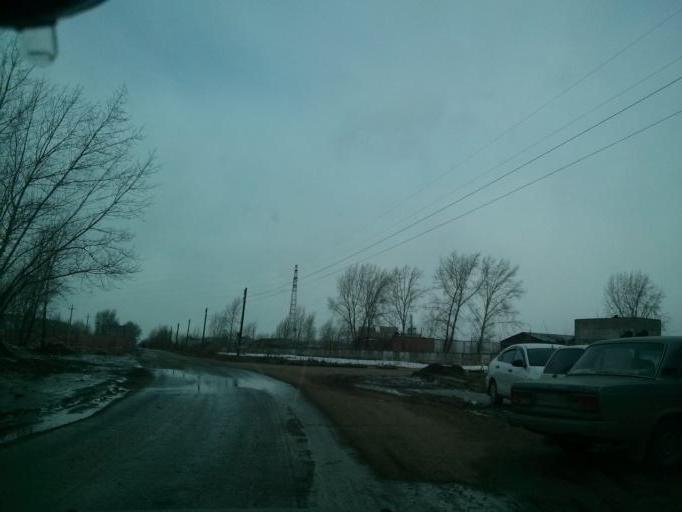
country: RU
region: Nizjnij Novgorod
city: Afonino
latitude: 56.2855
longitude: 44.1194
